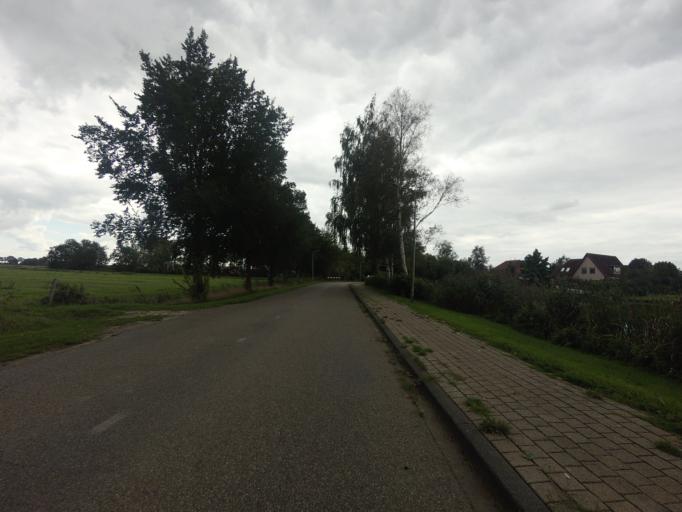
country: NL
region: Friesland
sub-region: Sudwest Fryslan
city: IJlst
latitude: 53.0082
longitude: 5.6337
